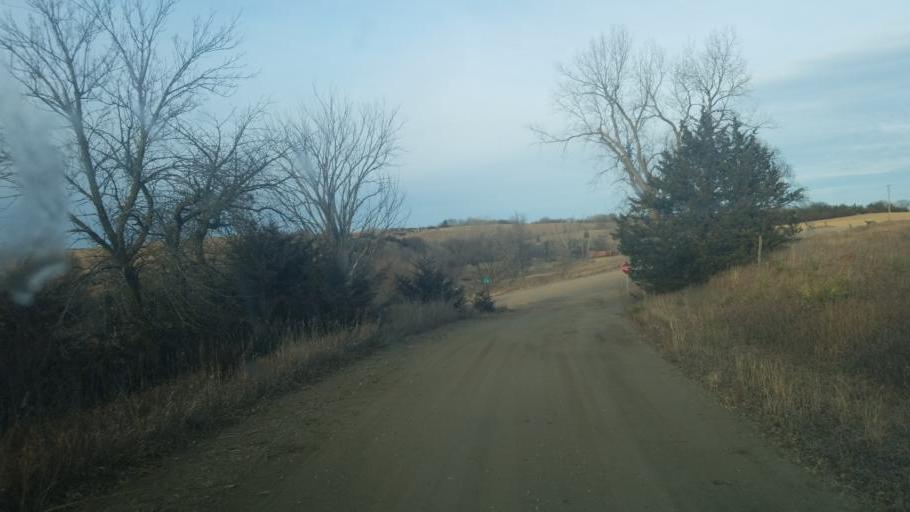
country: US
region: Nebraska
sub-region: Knox County
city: Center
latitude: 42.6837
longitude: -97.8184
